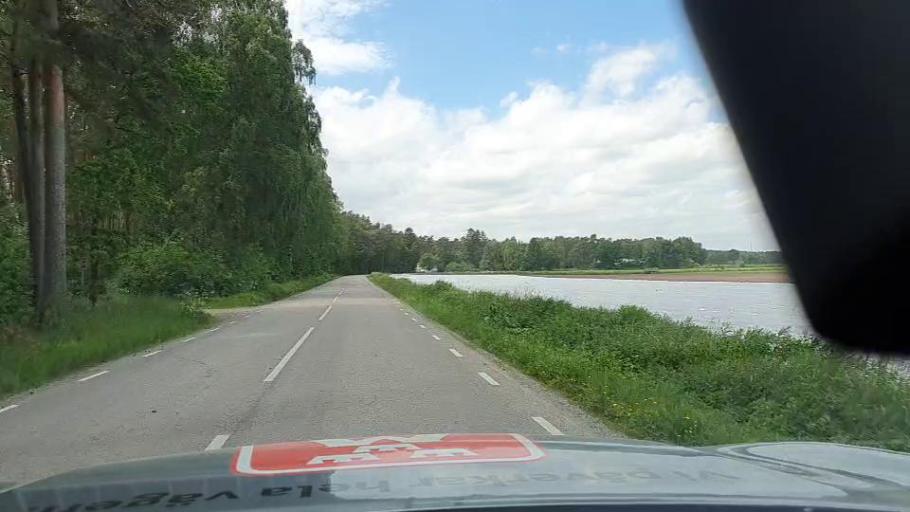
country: SE
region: Blekinge
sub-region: Karlshamns Kommun
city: Morrum
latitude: 56.0911
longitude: 14.7020
